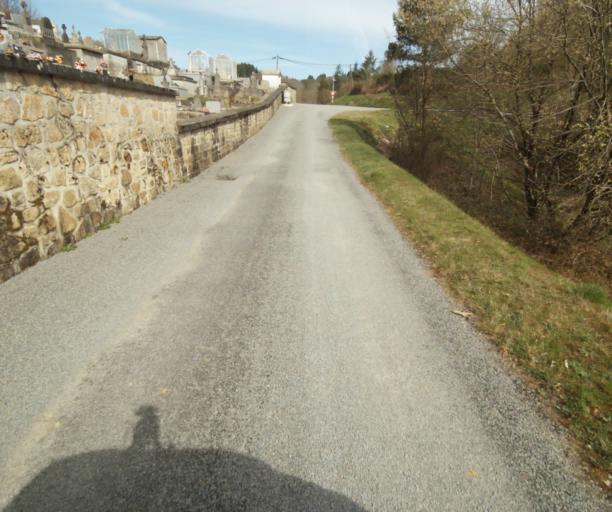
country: FR
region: Limousin
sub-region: Departement de la Correze
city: Naves
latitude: 45.3457
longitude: 1.8174
